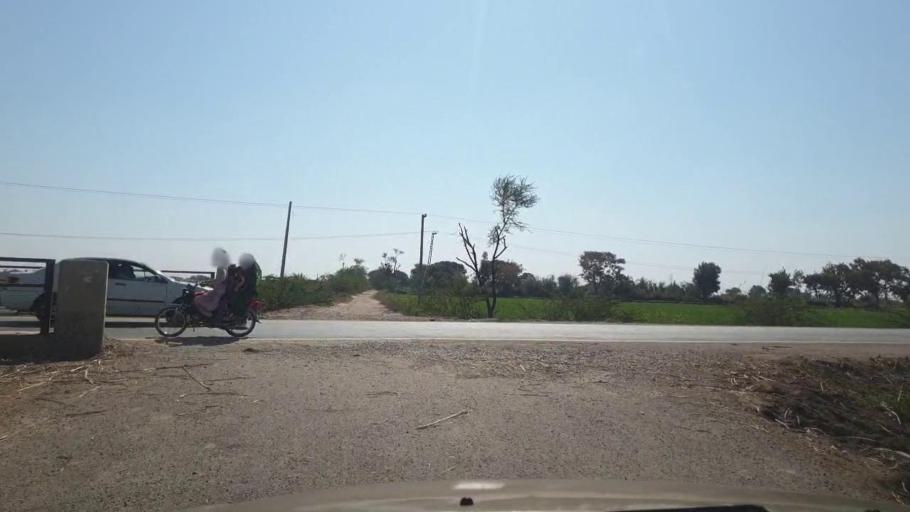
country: PK
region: Sindh
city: Mirpur Khas
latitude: 25.5673
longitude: 69.0625
